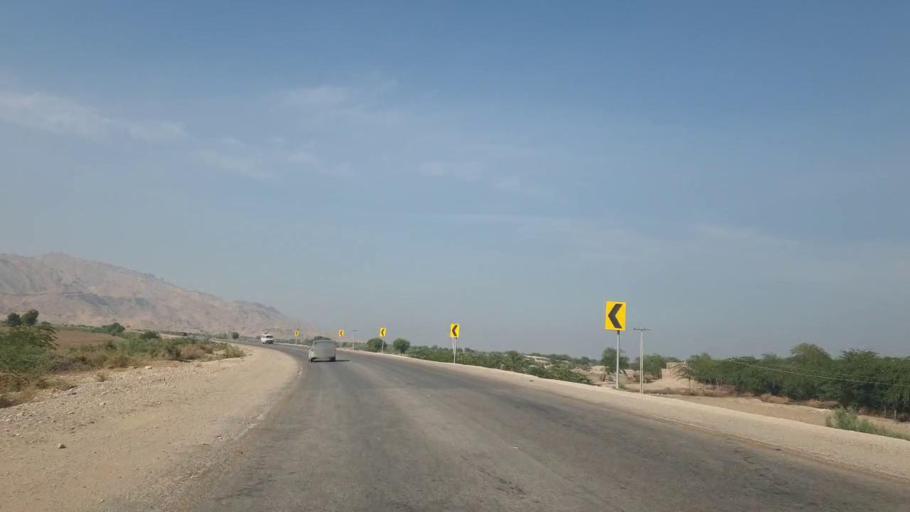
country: PK
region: Sindh
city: Sehwan
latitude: 26.2681
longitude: 67.9037
